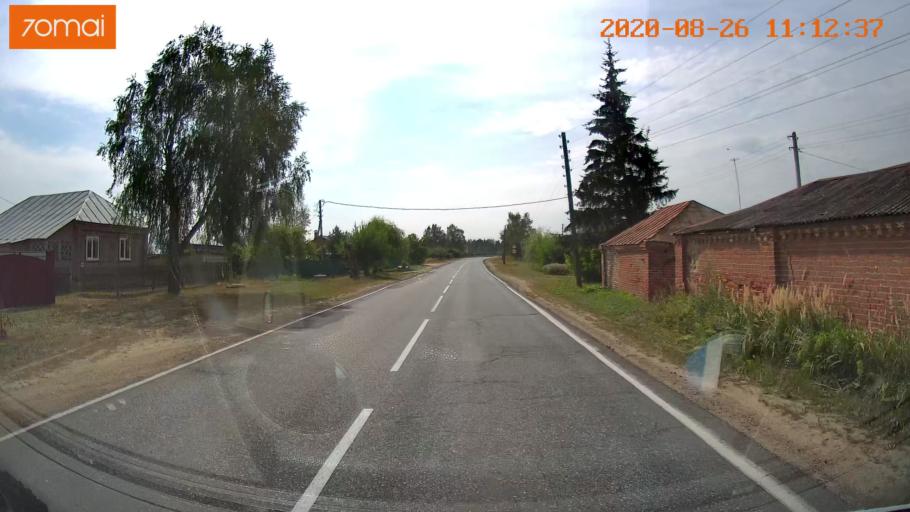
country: RU
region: Rjazan
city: Izhevskoye
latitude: 54.4684
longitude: 41.1248
